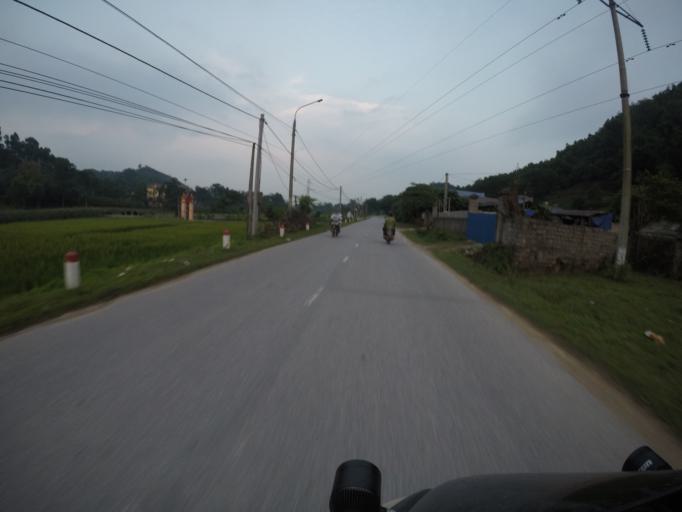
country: VN
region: Thai Nguyen
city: Chua Hang
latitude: 21.5888
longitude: 105.7306
